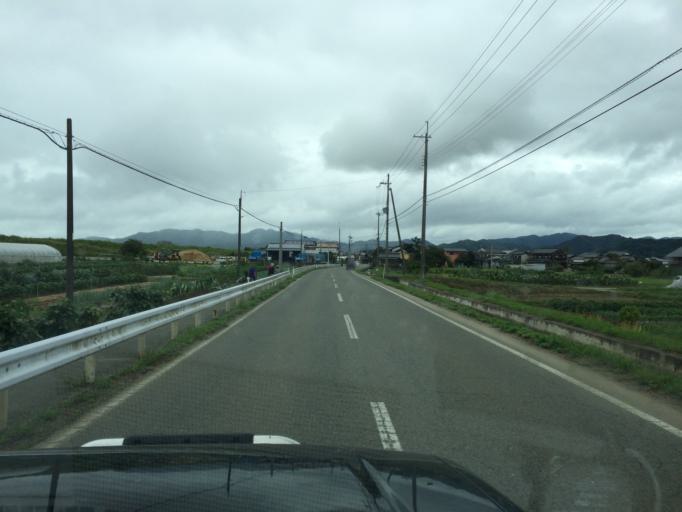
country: JP
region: Hyogo
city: Toyooka
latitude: 35.5071
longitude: 134.8234
